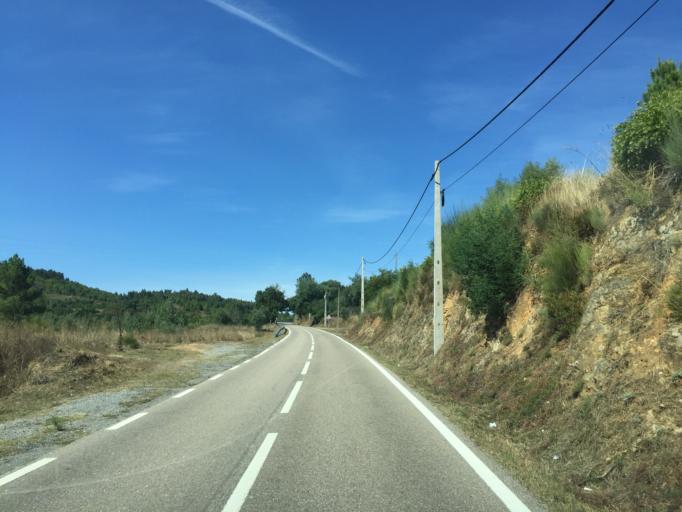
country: PT
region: Portalegre
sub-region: Marvao
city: Marvao
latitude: 39.3886
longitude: -7.3865
